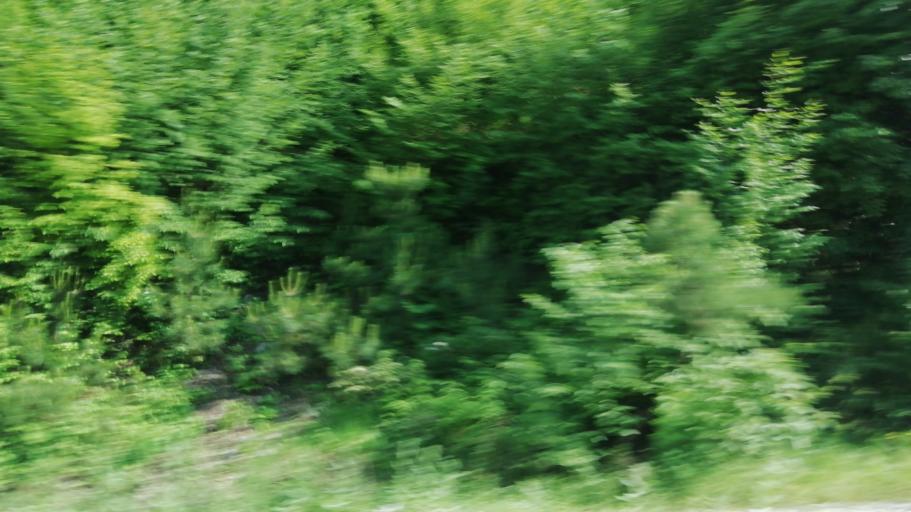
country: TR
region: Karabuk
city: Karabuk
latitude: 41.1242
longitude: 32.5891
